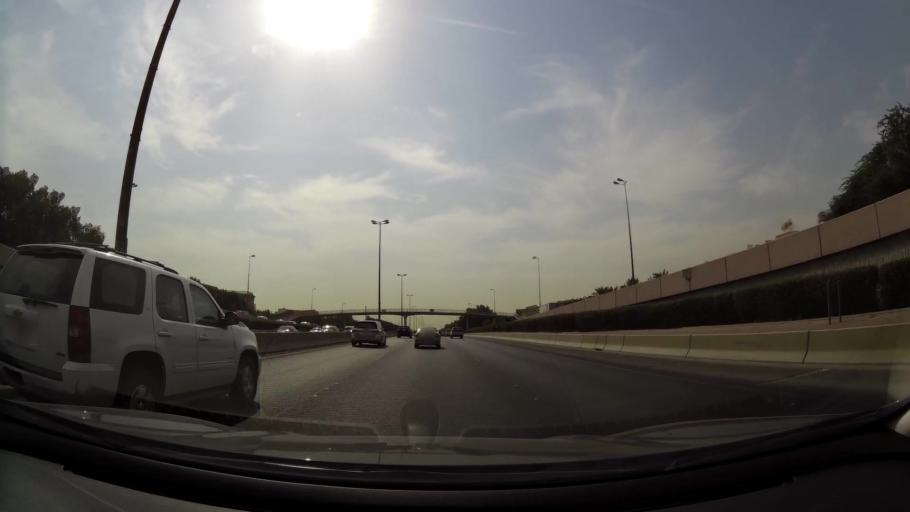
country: KW
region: Al Asimah
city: Ash Shamiyah
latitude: 29.3171
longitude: 47.9750
